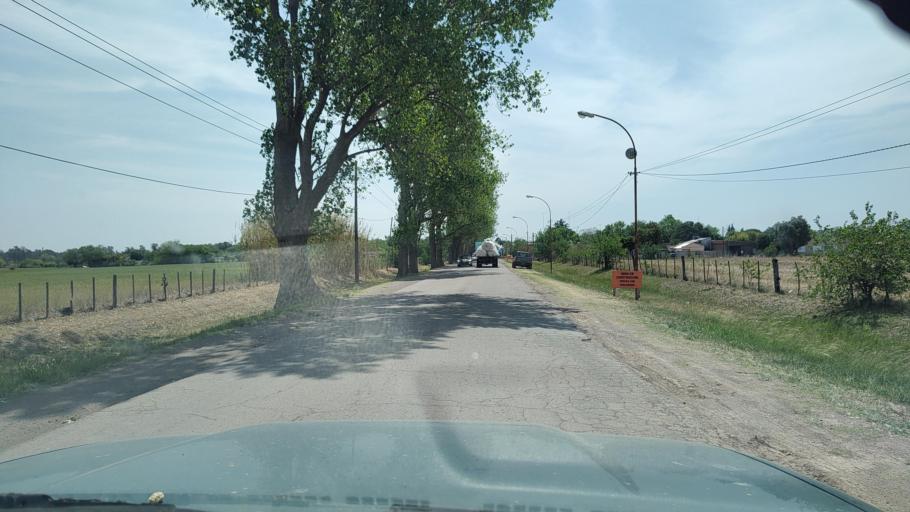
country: AR
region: Buenos Aires
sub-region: Partido de Lujan
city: Lujan
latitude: -34.6054
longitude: -59.1737
